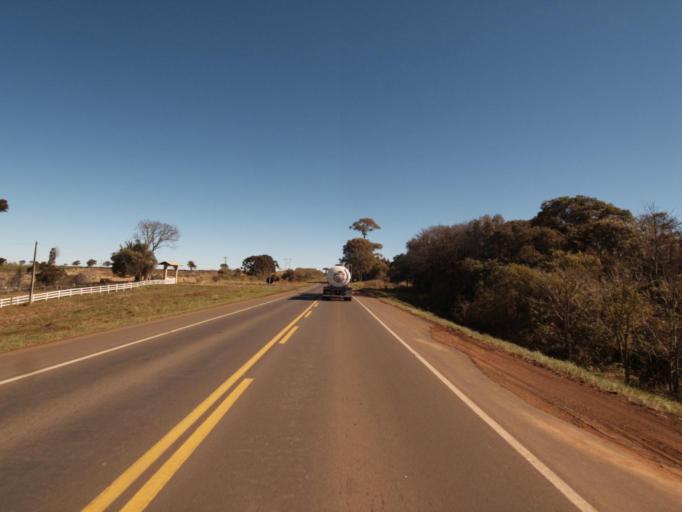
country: BR
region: Santa Catarina
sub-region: Xanxere
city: Xanxere
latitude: -26.8752
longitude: -52.3268
